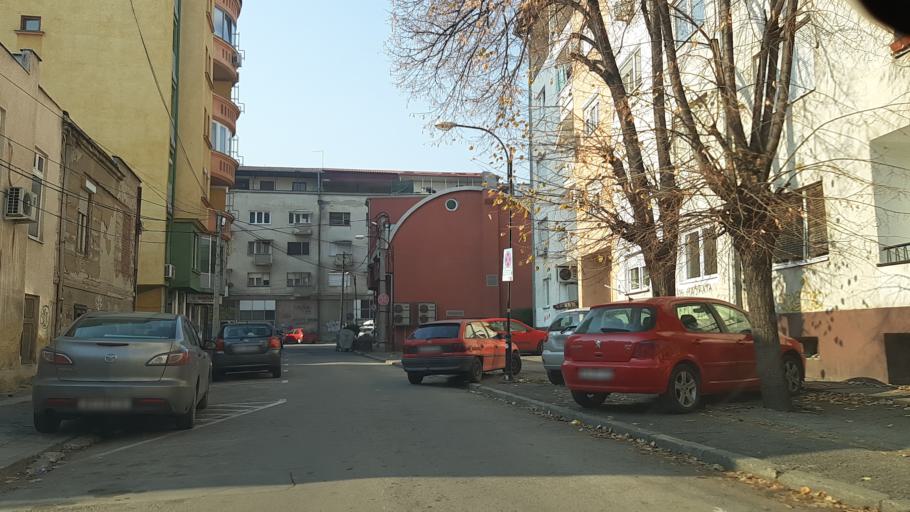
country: MK
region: Karpos
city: Skopje
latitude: 41.9967
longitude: 21.4196
